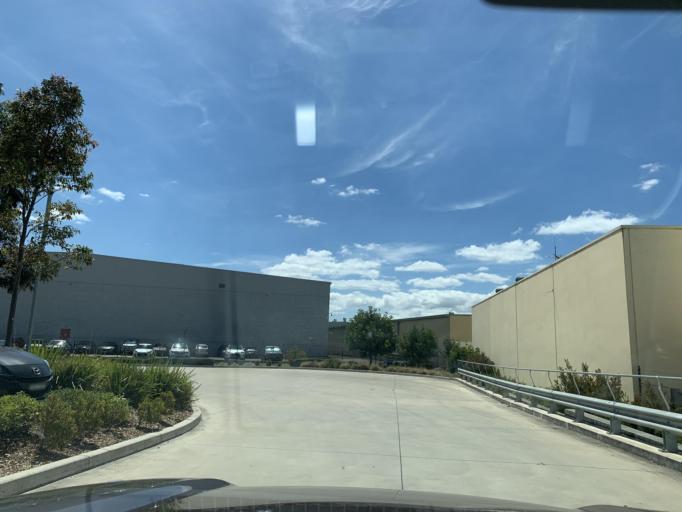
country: AU
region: New South Wales
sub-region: Holroyd
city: Girraween
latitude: -33.7688
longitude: 150.9521
